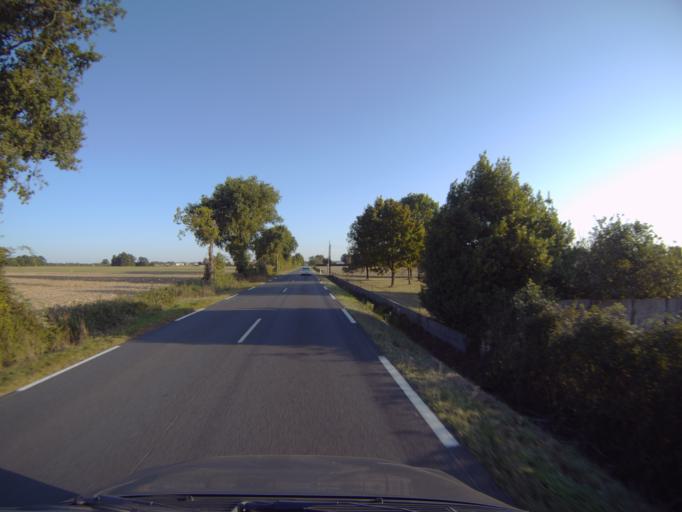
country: FR
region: Pays de la Loire
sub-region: Departement de la Vendee
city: Cugand
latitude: 47.0533
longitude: -1.2532
